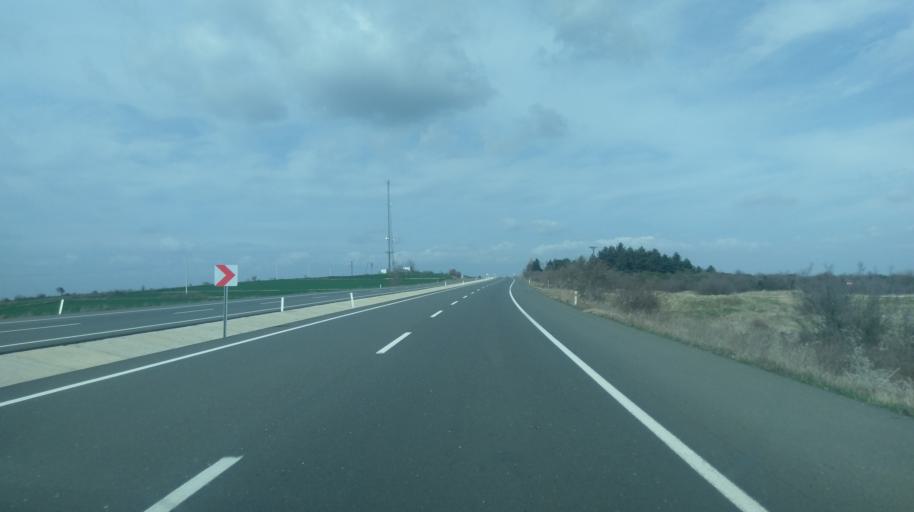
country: TR
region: Edirne
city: Hamidiye
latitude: 41.0708
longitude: 26.6393
